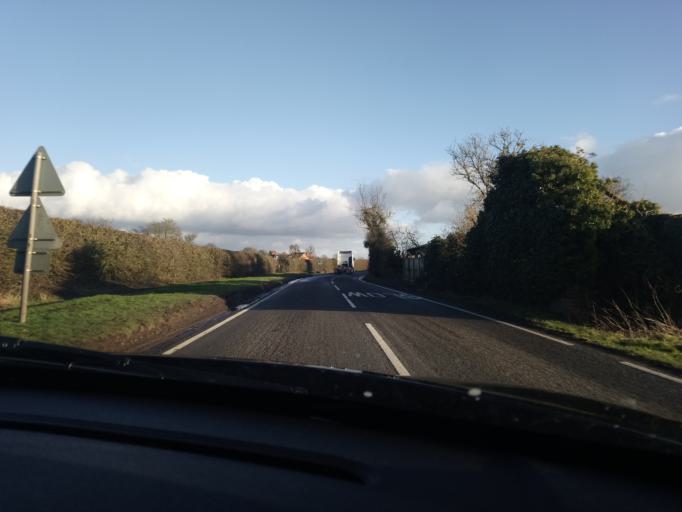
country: GB
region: England
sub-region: Shropshire
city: Ellesmere
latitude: 52.9138
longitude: -2.9132
